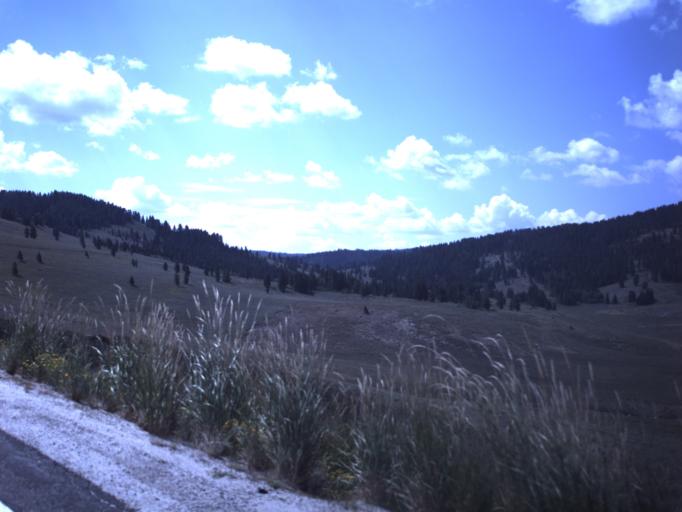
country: US
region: Idaho
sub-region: Bear Lake County
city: Paris
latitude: 41.9293
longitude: -111.4788
